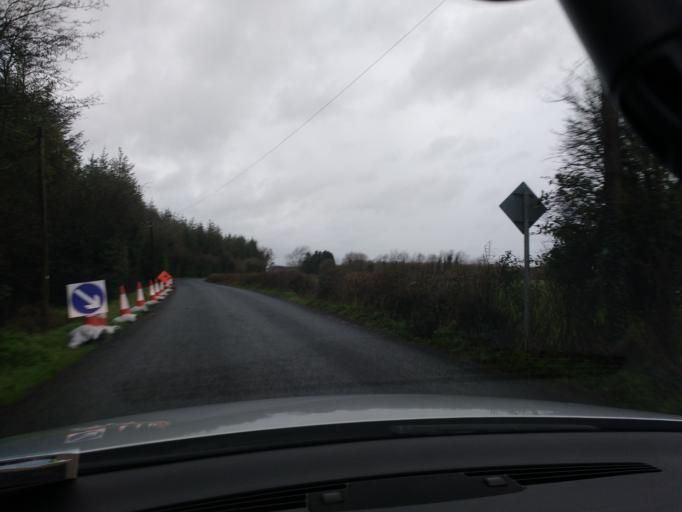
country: IE
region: Leinster
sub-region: Laois
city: Rathdowney
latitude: 52.6935
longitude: -7.6275
